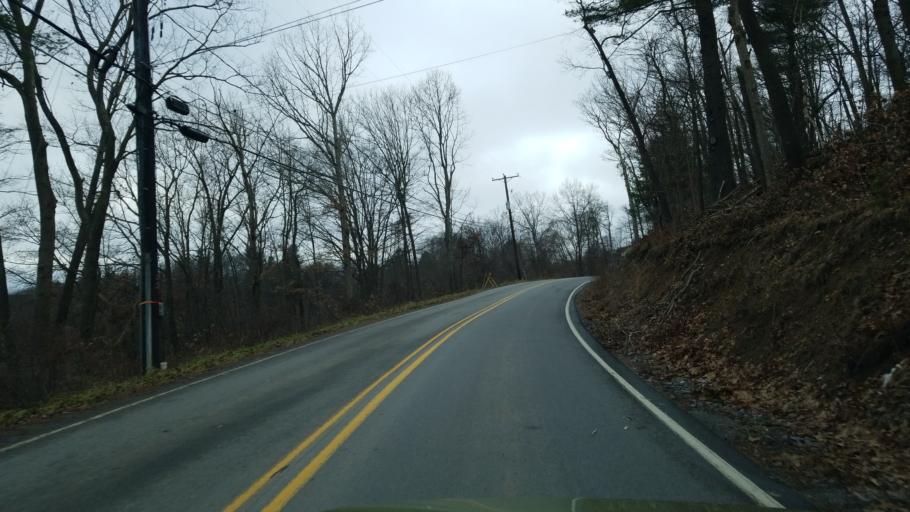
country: US
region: Pennsylvania
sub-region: Clearfield County
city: Clearfield
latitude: 41.0333
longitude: -78.4644
